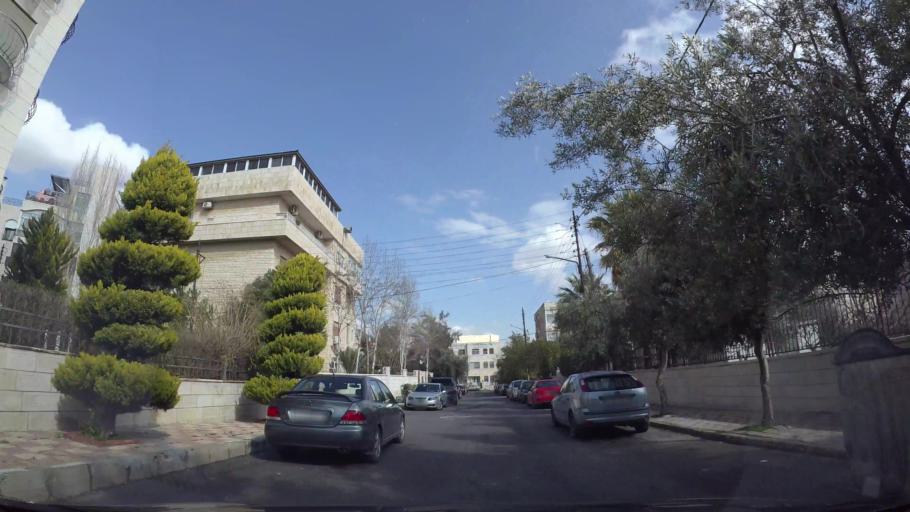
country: JO
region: Amman
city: Amman
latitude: 31.9689
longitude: 35.8924
